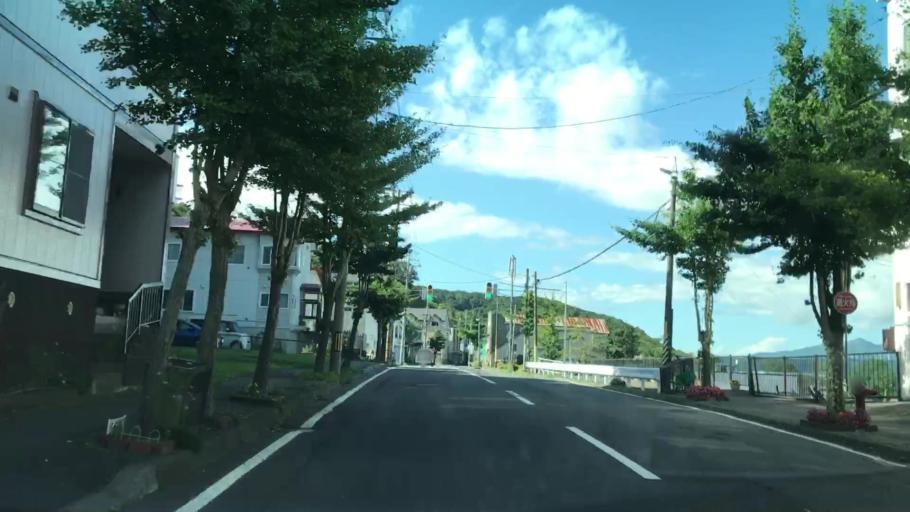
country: JP
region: Hokkaido
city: Muroran
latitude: 42.3211
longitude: 140.9700
